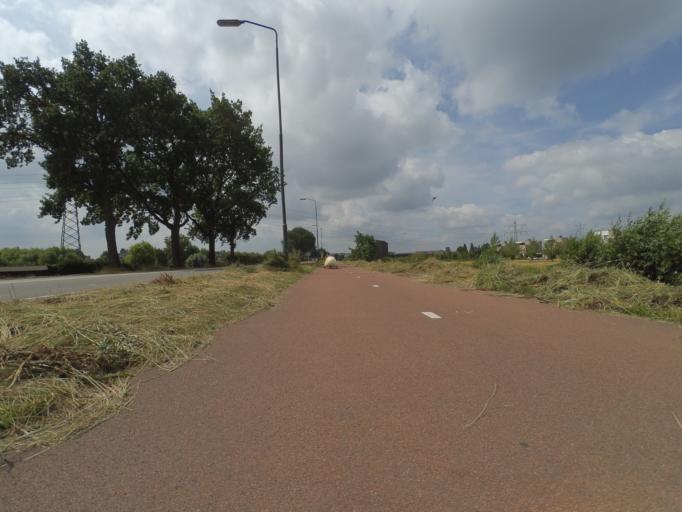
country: NL
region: North Brabant
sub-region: Gemeente Geertruidenberg
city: Geertruidenberg
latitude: 51.7052
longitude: 4.8755
